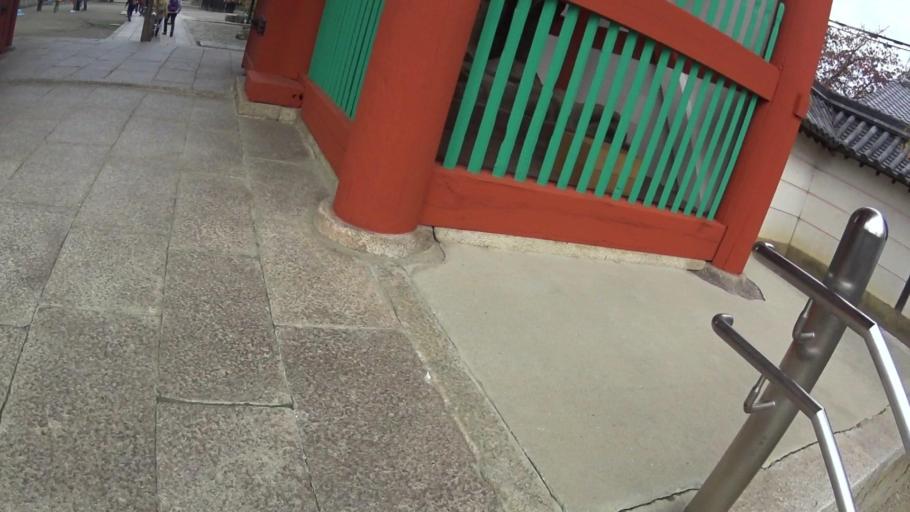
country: JP
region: Osaka
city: Kashihara
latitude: 34.5693
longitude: 135.5967
